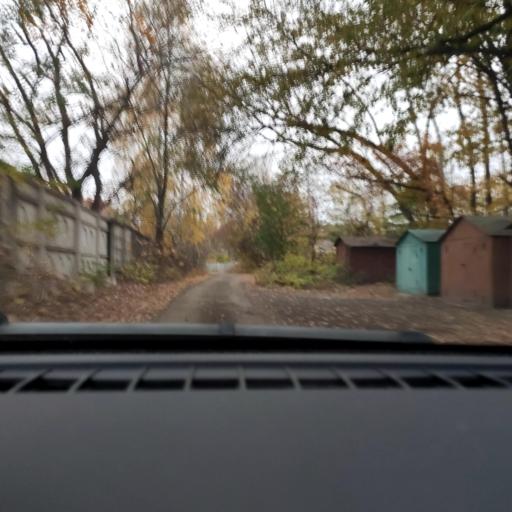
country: RU
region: Voronezj
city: Voronezh
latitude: 51.7172
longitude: 39.2319
